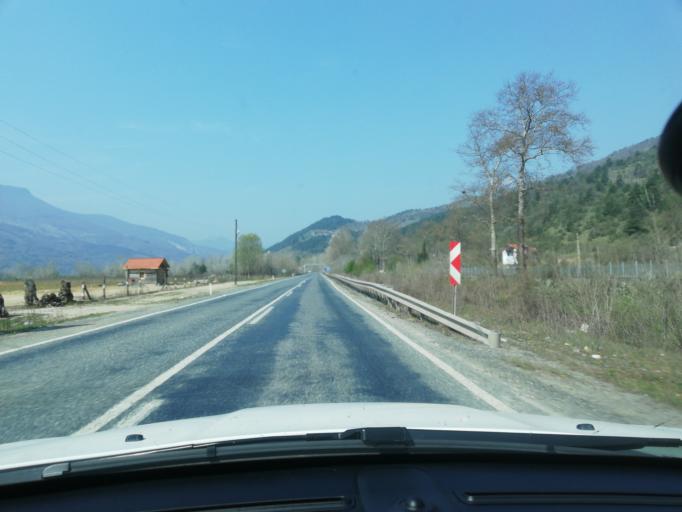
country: TR
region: Karabuk
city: Yenice
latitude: 41.2170
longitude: 32.3009
